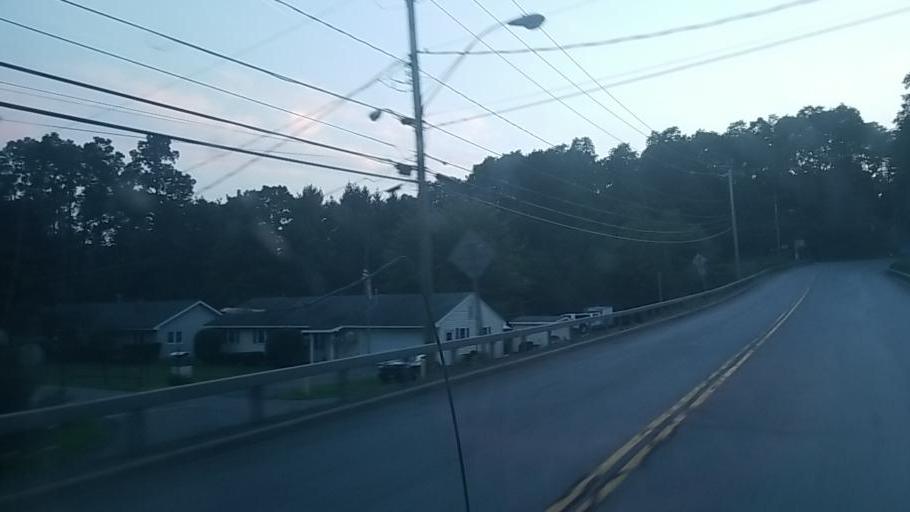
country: US
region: New York
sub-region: Montgomery County
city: Fonda
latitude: 42.9575
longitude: -74.3813
